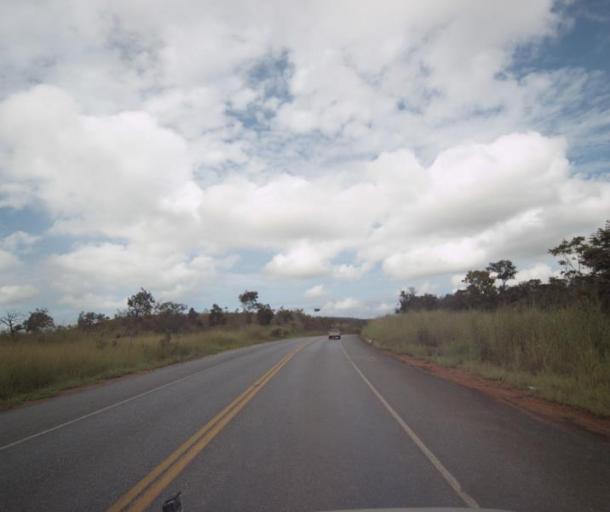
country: BR
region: Goias
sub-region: Pirenopolis
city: Pirenopolis
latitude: -15.6041
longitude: -48.6453
